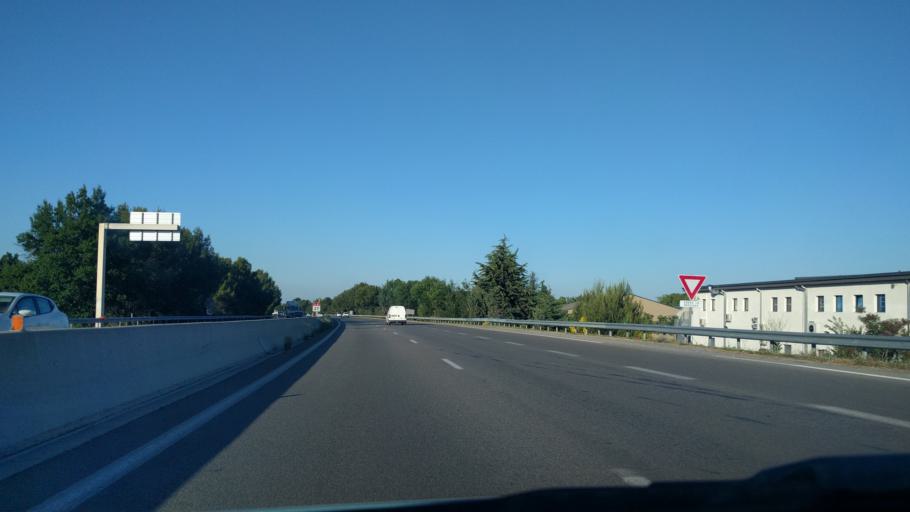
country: FR
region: Provence-Alpes-Cote d'Azur
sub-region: Departement des Bouches-du-Rhone
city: Venelles
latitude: 43.5916
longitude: 5.4816
